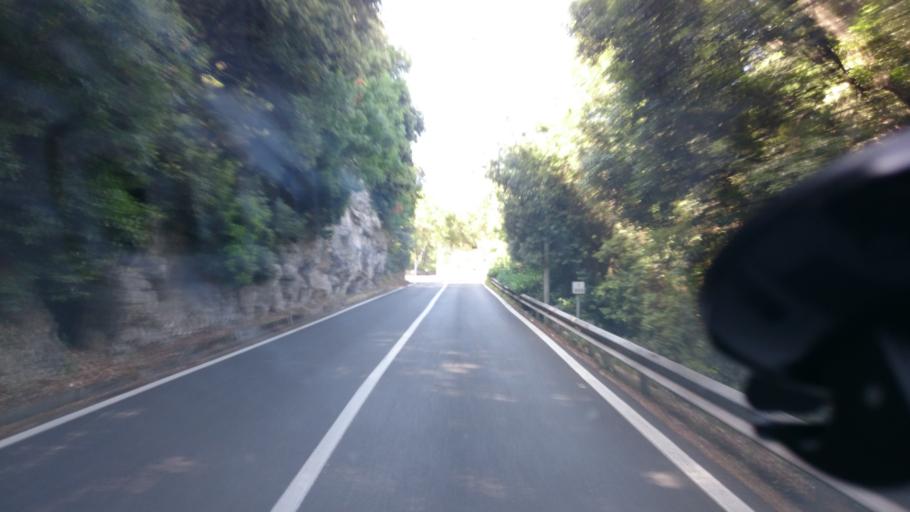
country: IT
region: Basilicate
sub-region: Provincia di Potenza
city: Maratea
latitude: 39.9939
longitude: 15.7067
